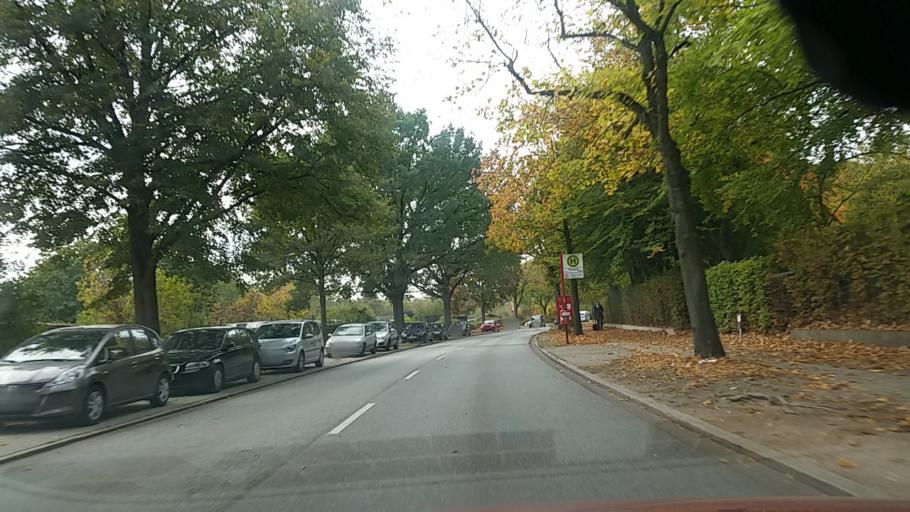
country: DE
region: Hamburg
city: Ohlsdorf
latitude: 53.6195
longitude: 10.0231
